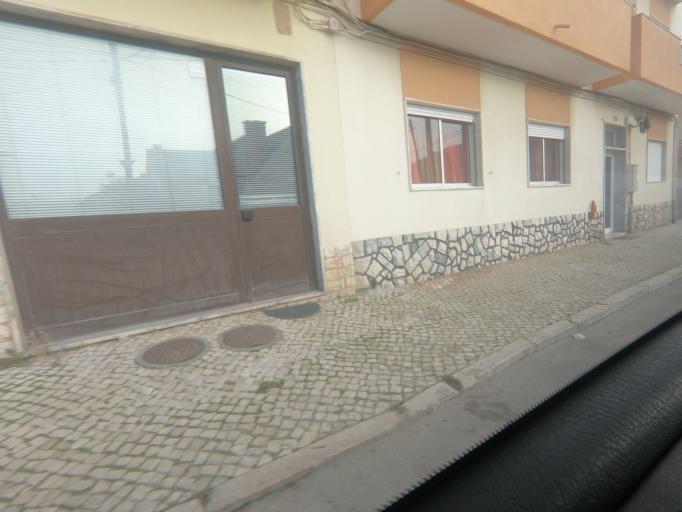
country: PT
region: Setubal
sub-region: Palmela
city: Pinhal Novo
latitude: 38.6370
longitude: -8.9162
